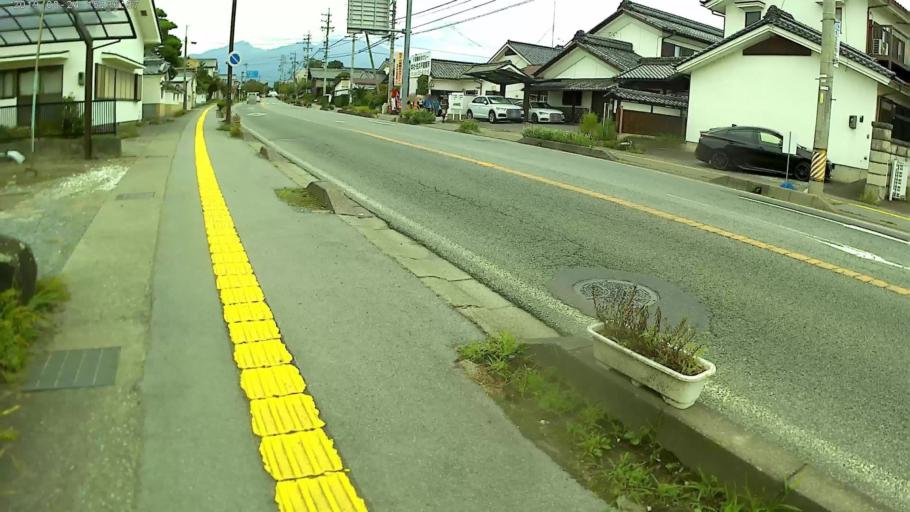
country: JP
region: Nagano
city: Saku
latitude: 36.2764
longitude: 138.4782
